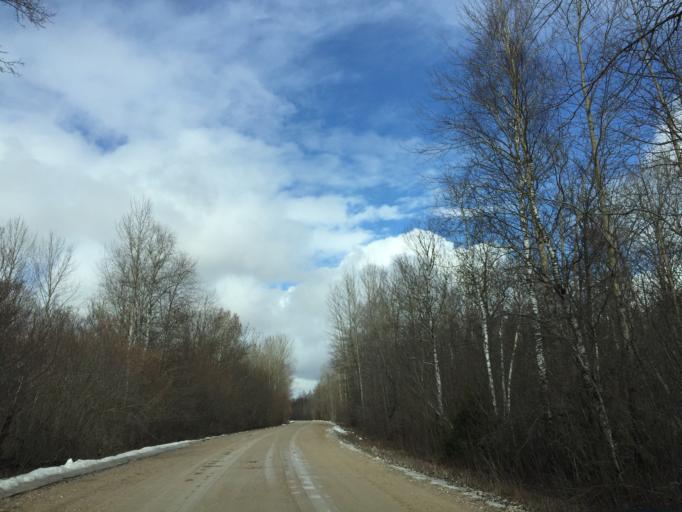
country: EE
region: Laeaene
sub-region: Lihula vald
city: Lihula
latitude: 58.7230
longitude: 23.8298
